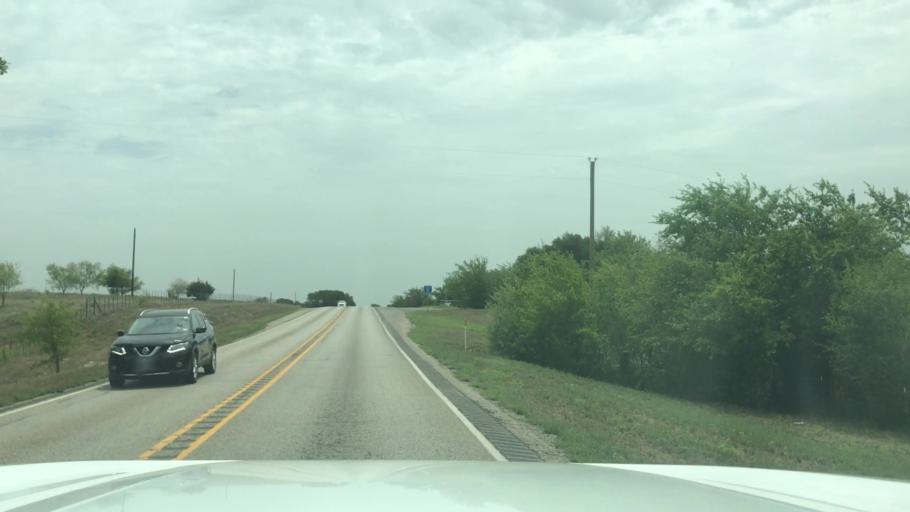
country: US
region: Texas
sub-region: Hamilton County
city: Hico
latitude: 32.0472
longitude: -98.1500
